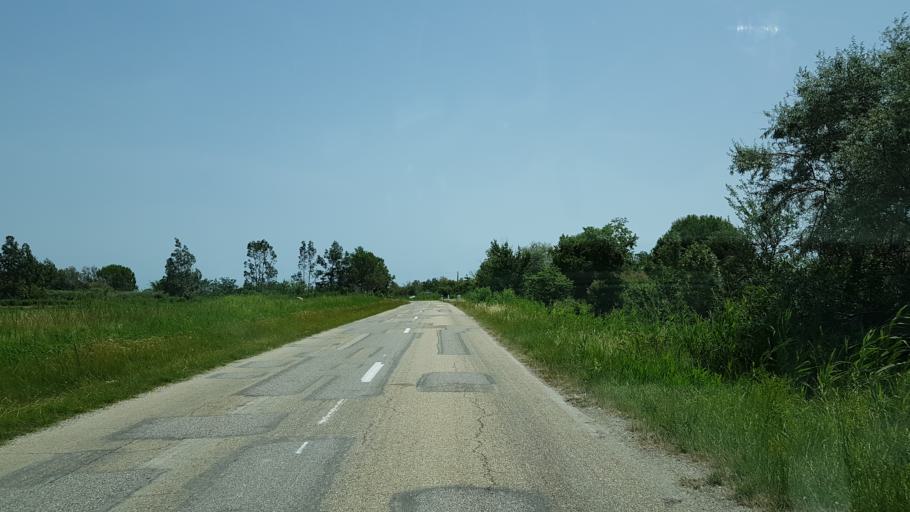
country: FR
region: Provence-Alpes-Cote d'Azur
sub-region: Departement des Bouches-du-Rhone
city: Port-Saint-Louis-du-Rhone
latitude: 43.4298
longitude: 4.6927
